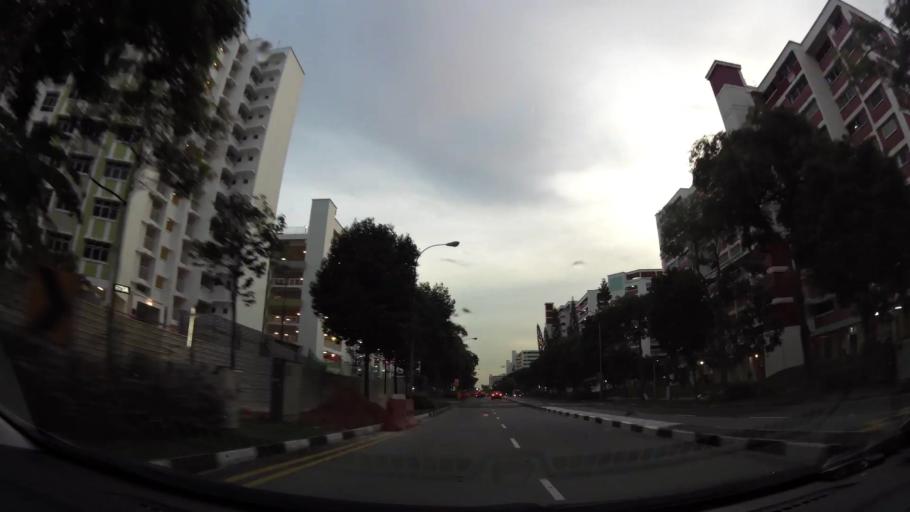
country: MY
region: Johor
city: Kampung Pasir Gudang Baru
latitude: 1.4205
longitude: 103.8416
